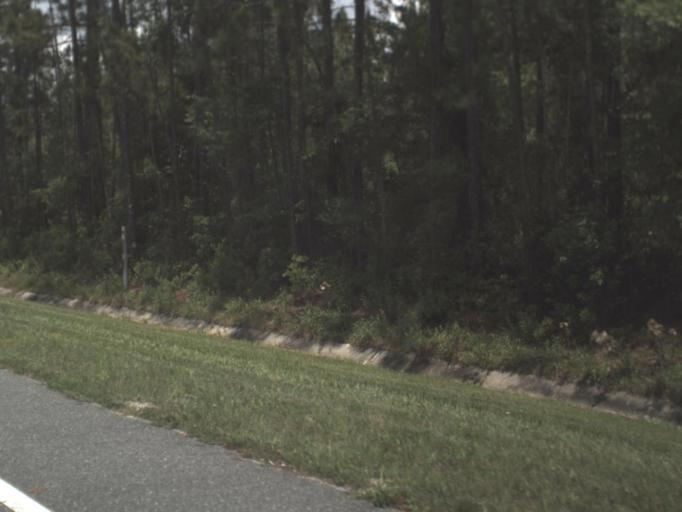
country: US
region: Florida
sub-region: Columbia County
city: Watertown
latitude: 30.1454
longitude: -82.5451
